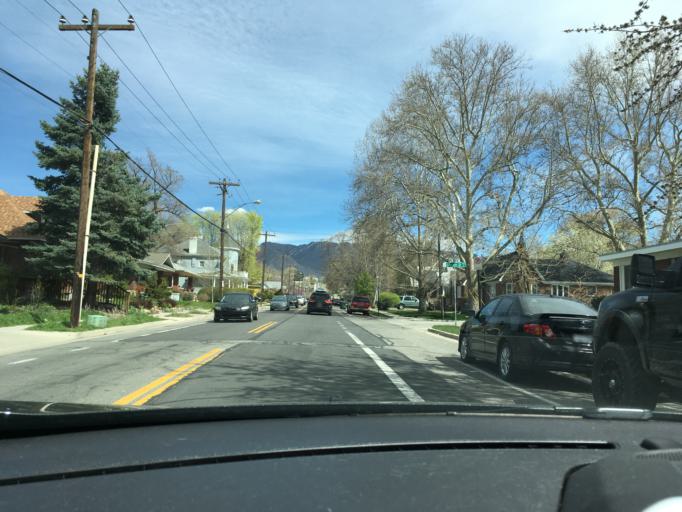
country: US
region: Utah
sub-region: Salt Lake County
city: Salt Lake City
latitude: 40.7416
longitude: -111.8644
